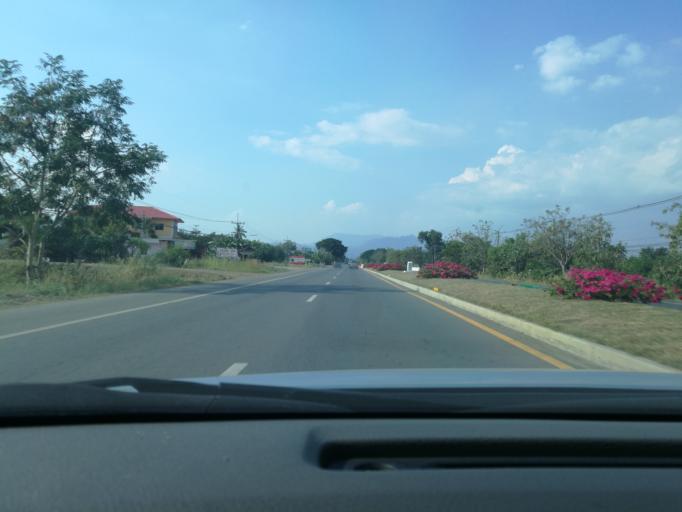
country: TH
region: Phetchabun
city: Phetchabun
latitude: 16.2292
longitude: 101.0860
